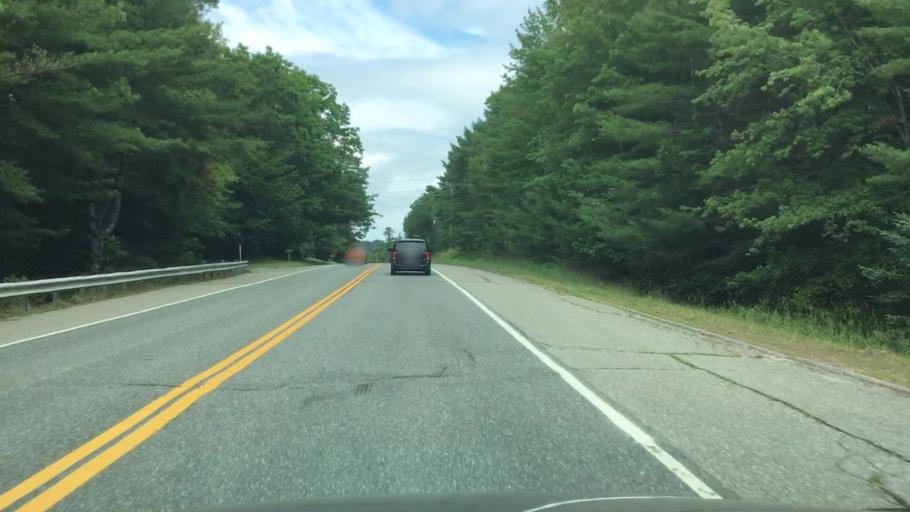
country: US
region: Maine
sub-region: Hancock County
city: Orland
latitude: 44.5617
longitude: -68.6984
